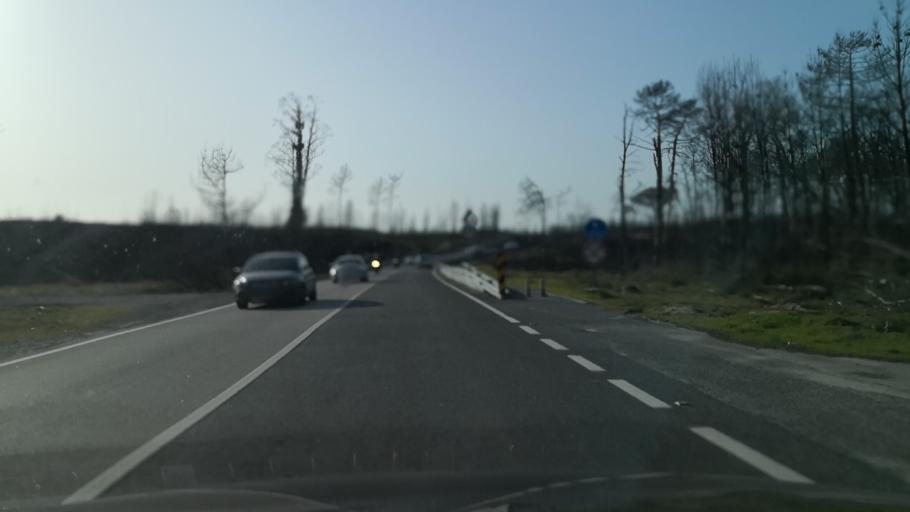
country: PT
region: Leiria
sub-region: Marinha Grande
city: Marinha Grande
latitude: 39.7468
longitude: -8.9739
